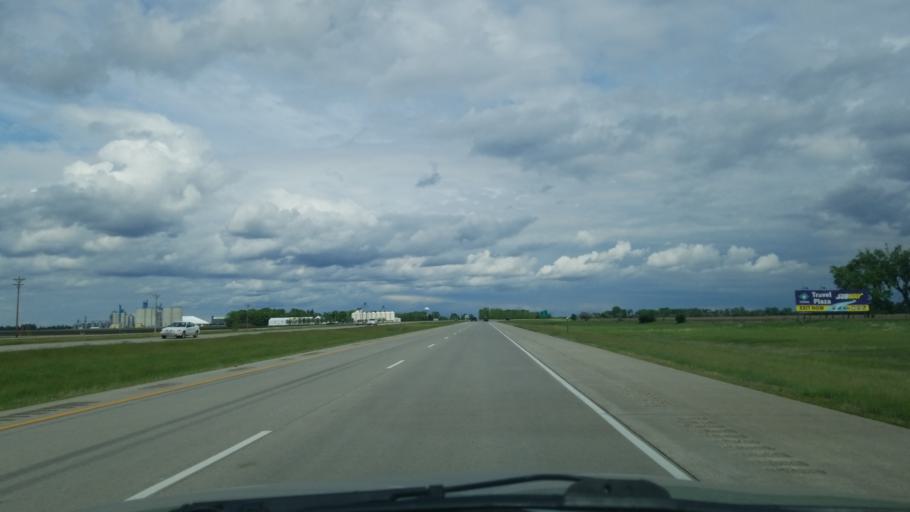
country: US
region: North Dakota
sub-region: Cass County
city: Casselton
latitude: 46.8759
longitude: -97.2444
